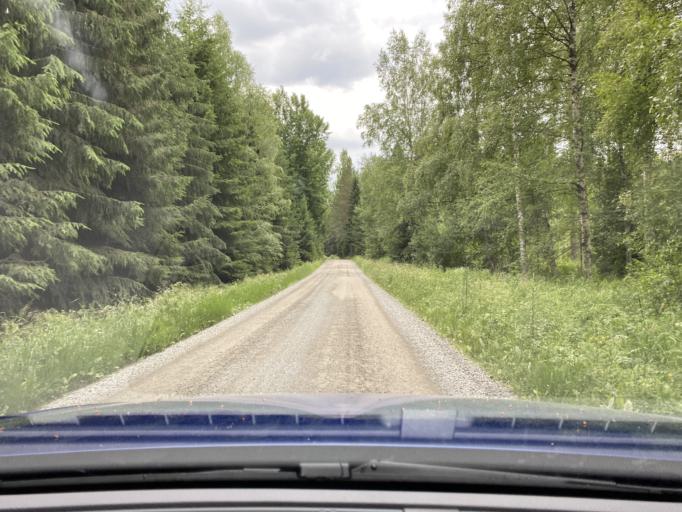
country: FI
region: Satakunta
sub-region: Rauma
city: Lappi
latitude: 61.1459
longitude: 21.9078
